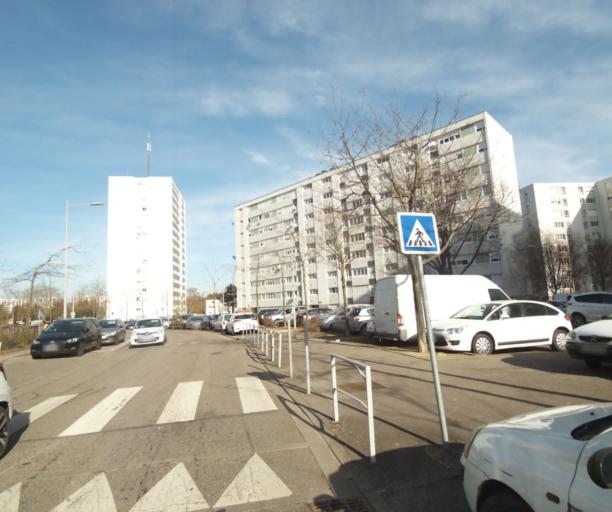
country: FR
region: Lorraine
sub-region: Departement de Meurthe-et-Moselle
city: Vandoeuvre-les-Nancy
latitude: 48.6611
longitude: 6.1824
